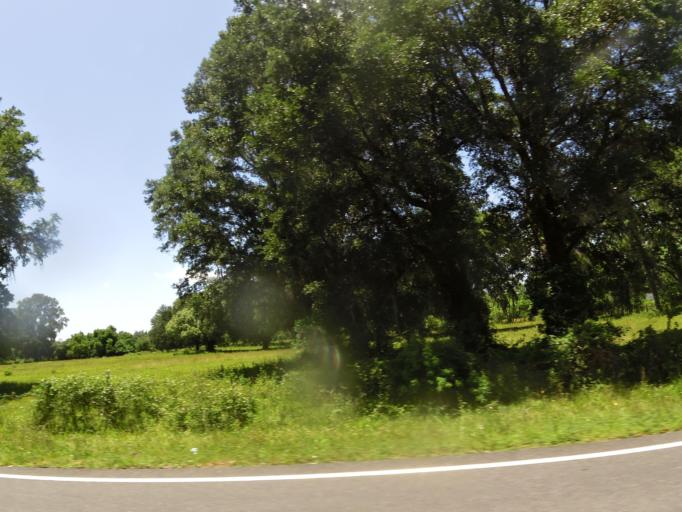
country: US
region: Florida
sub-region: Union County
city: Lake Butler
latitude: 30.0582
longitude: -82.2367
